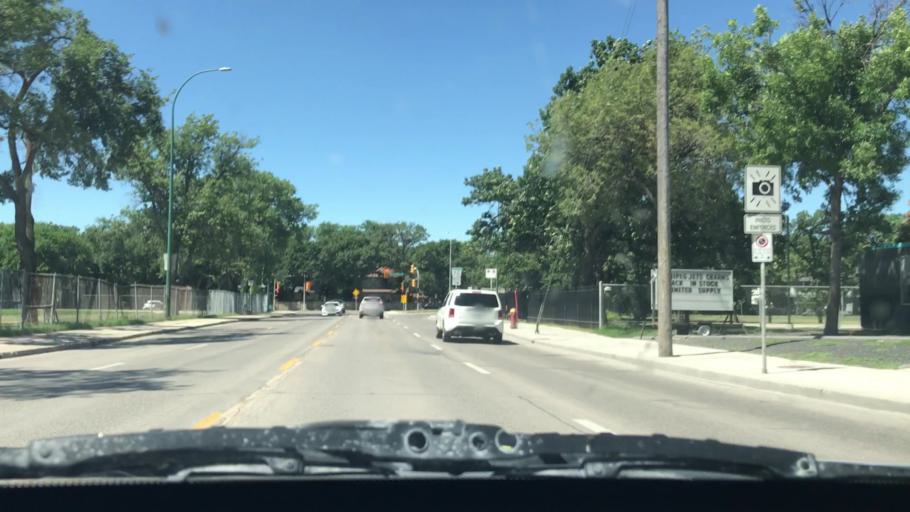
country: CA
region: Manitoba
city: Winnipeg
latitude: 49.8740
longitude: -97.1663
